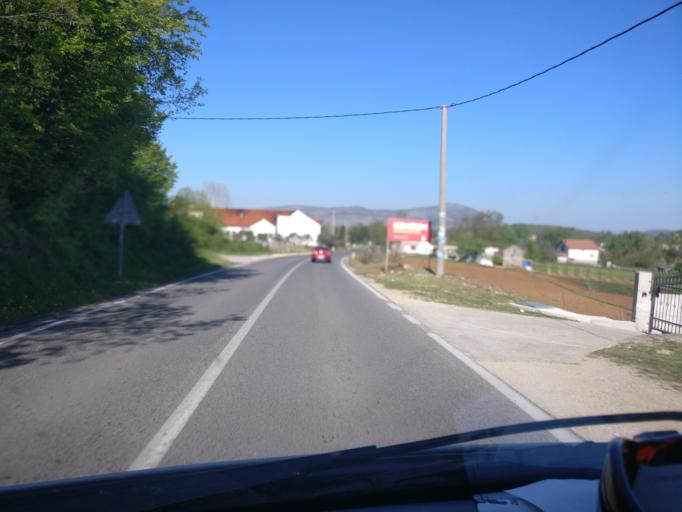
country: BA
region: Federation of Bosnia and Herzegovina
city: Tasovcici
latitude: 43.1361
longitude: 17.7872
